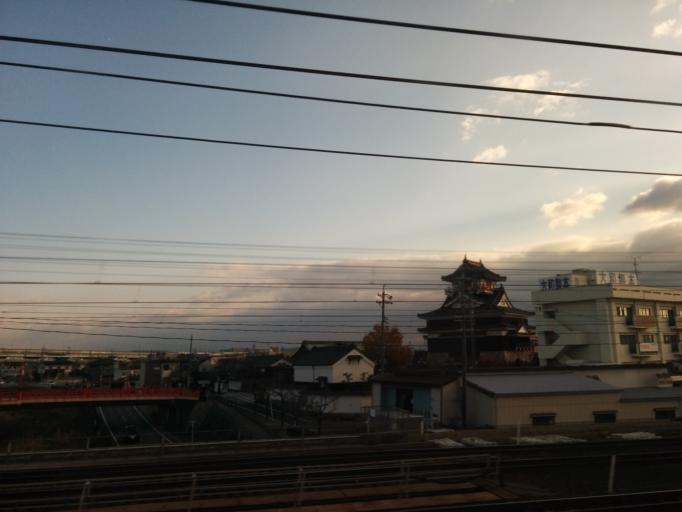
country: JP
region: Aichi
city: Inazawa
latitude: 35.2165
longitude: 136.8421
